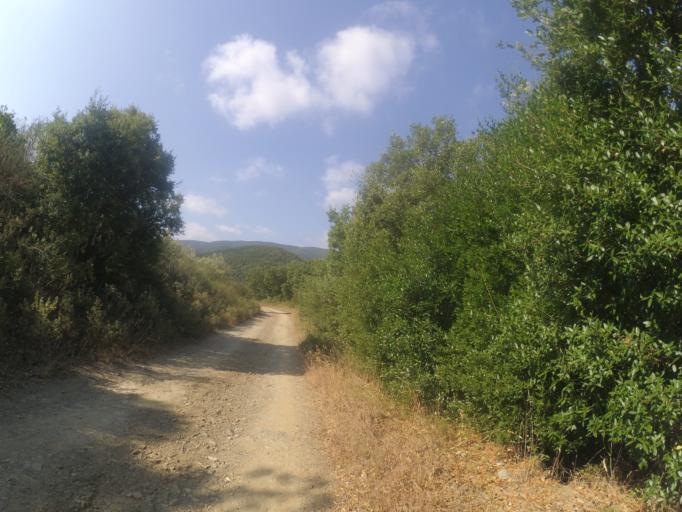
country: FR
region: Languedoc-Roussillon
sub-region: Departement des Pyrenees-Orientales
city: Ille-sur-Tet
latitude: 42.6461
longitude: 2.6268
